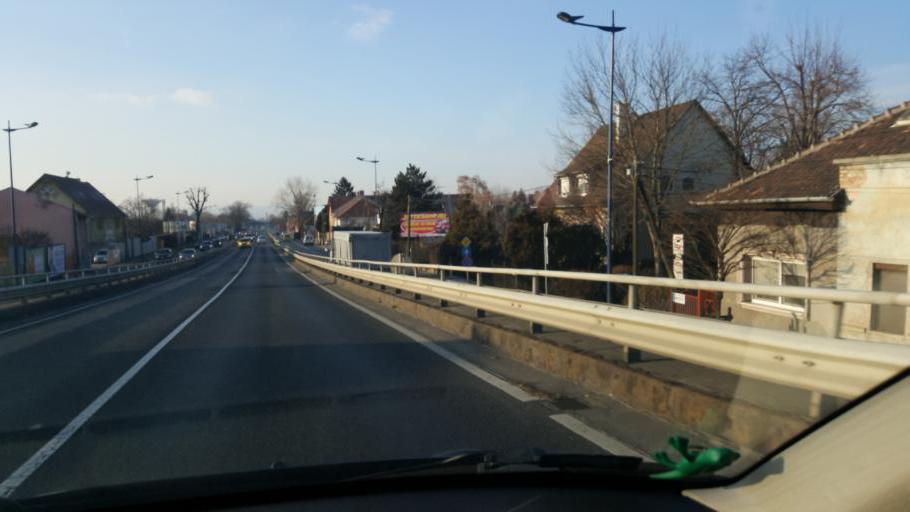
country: HU
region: Budapest
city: Budapest XVIII. keruelet
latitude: 47.4535
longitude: 19.1943
